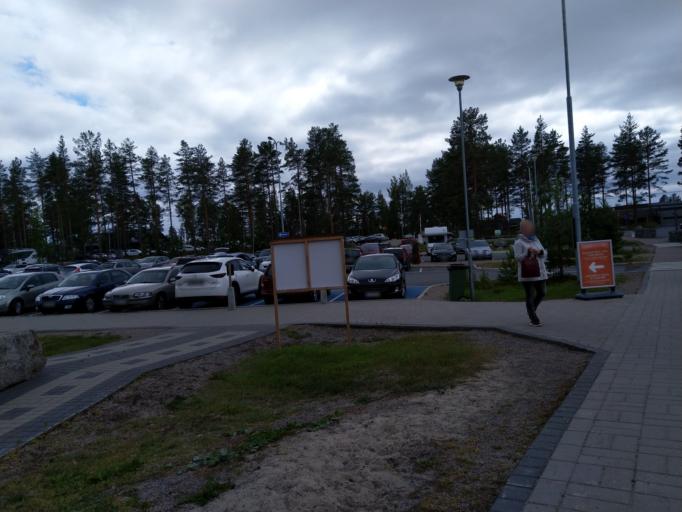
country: FI
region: Southern Ostrobothnia
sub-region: Kuusiokunnat
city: AEhtaeri
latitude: 62.5361
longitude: 24.1844
